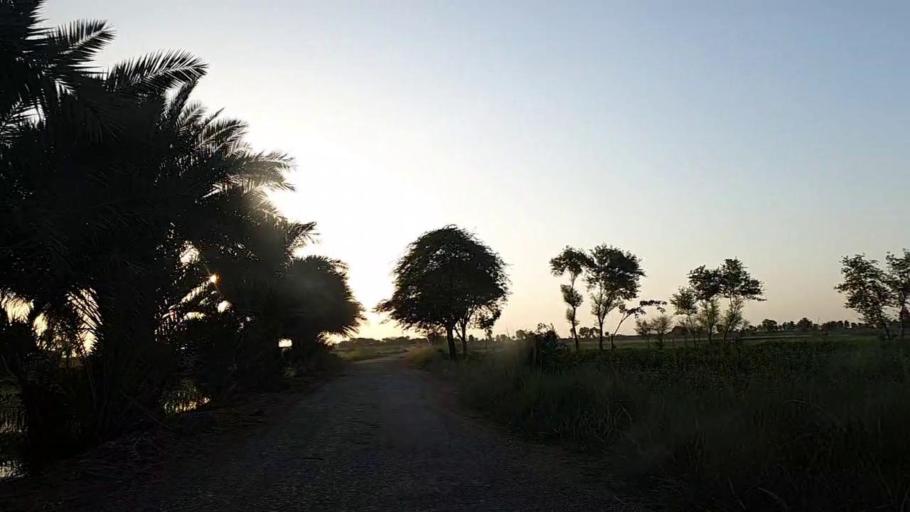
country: PK
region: Sindh
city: Hingorja
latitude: 27.0593
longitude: 68.3980
